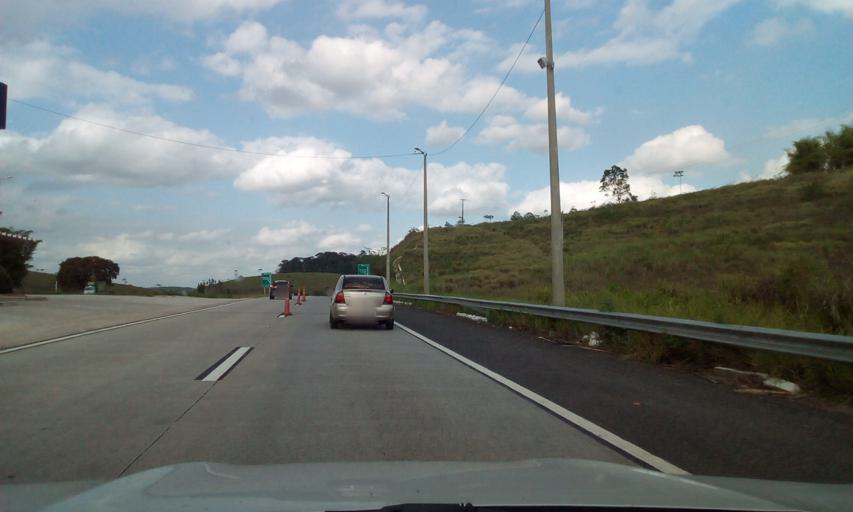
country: BR
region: Pernambuco
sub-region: Joaquim Nabuco
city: Joaquim Nabuco
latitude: -8.5734
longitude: -35.4809
